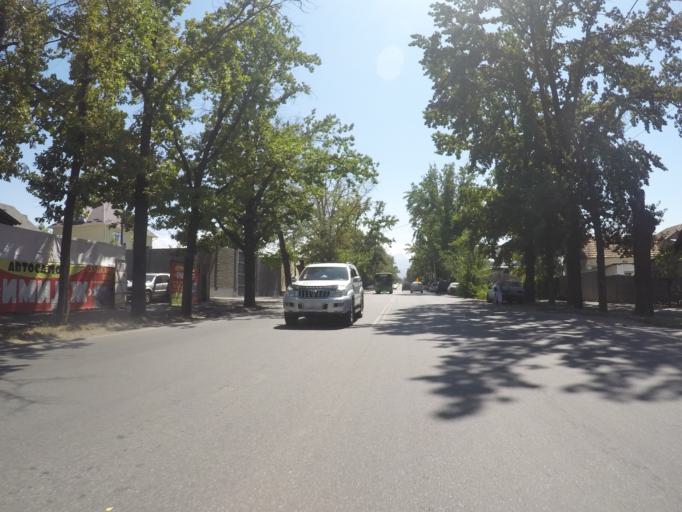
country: KG
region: Chuy
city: Bishkek
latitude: 42.8511
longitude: 74.5770
